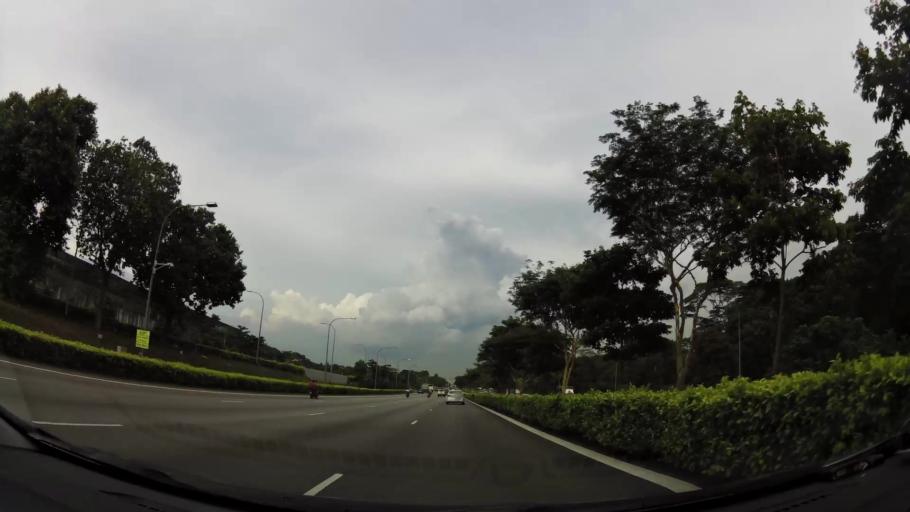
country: MY
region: Johor
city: Johor Bahru
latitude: 1.3745
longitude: 103.7273
